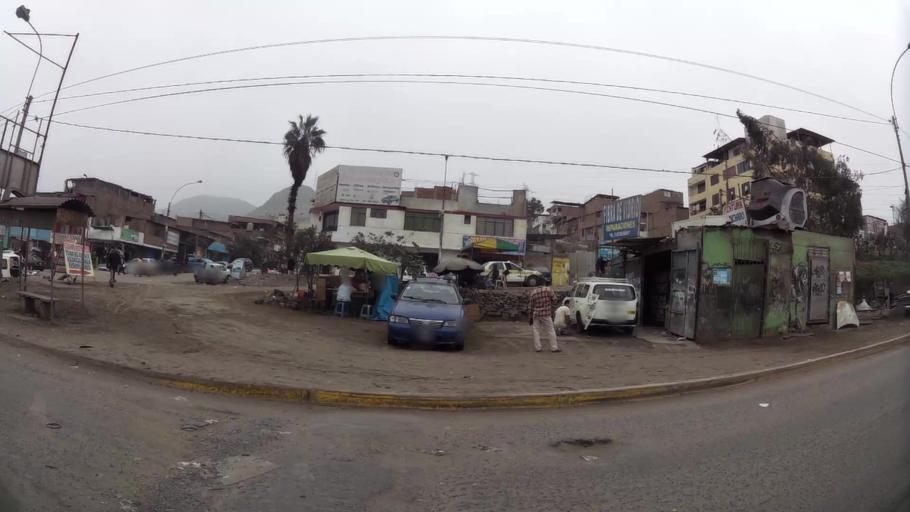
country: PE
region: Lima
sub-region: Lima
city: Surco
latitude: -12.1787
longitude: -76.9445
